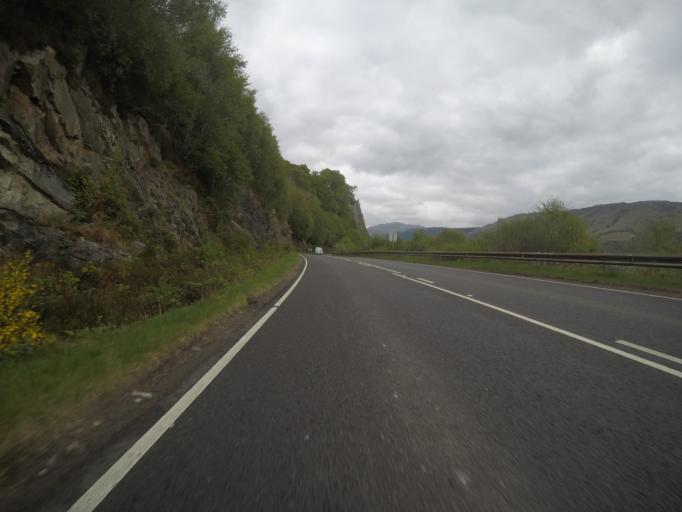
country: GB
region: Scotland
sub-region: Highland
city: Fort William
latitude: 57.2701
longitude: -5.5083
